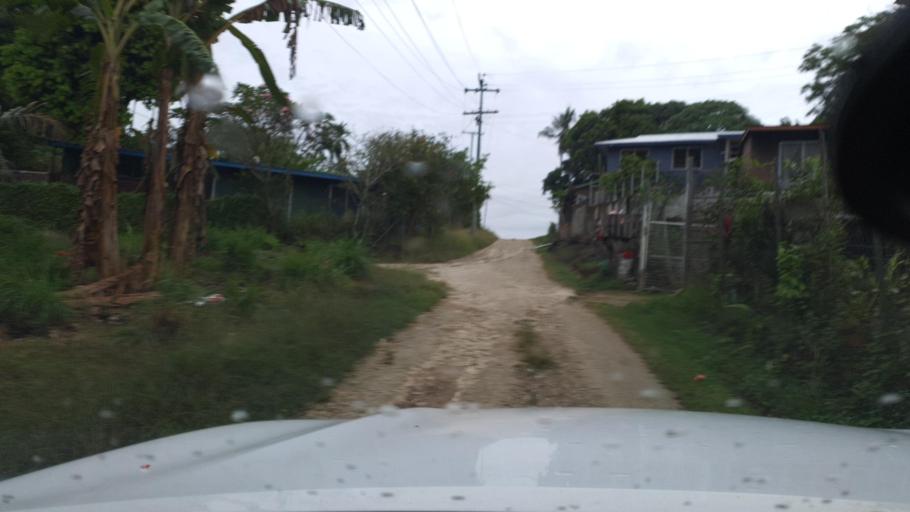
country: SB
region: Guadalcanal
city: Honiara
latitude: -9.4478
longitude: 159.9841
